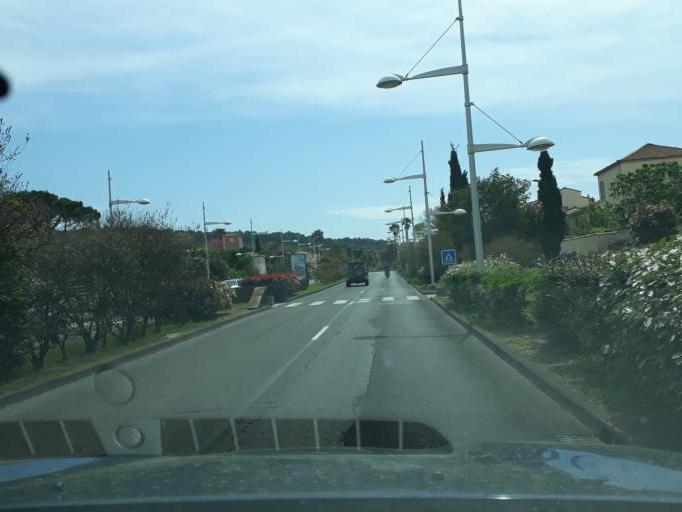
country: FR
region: Languedoc-Roussillon
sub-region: Departement de l'Herault
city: Agde
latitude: 43.3006
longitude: 3.4903
